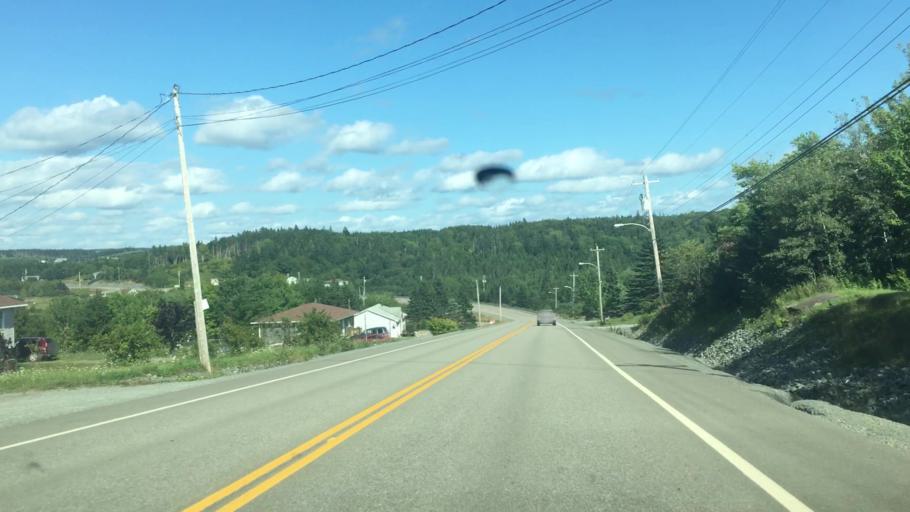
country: CA
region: Nova Scotia
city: Princeville
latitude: 45.6844
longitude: -60.7599
